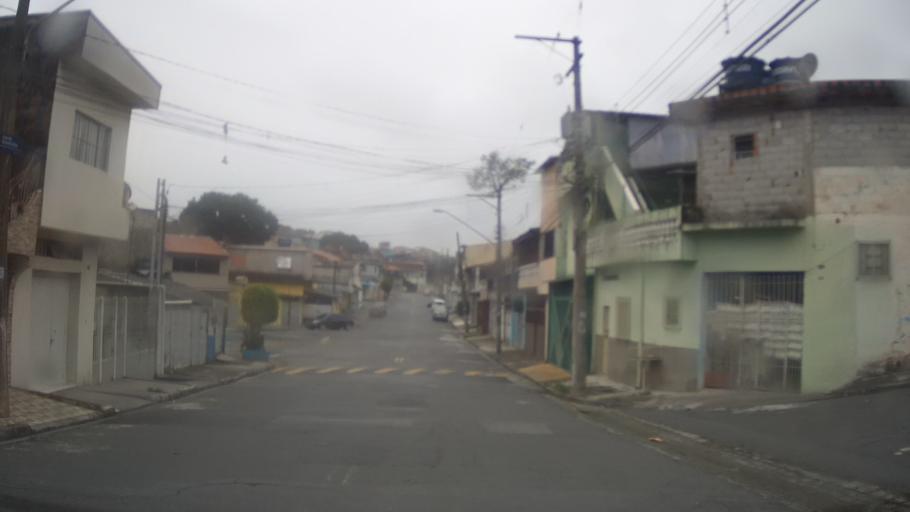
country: BR
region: Sao Paulo
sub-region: Guarulhos
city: Guarulhos
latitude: -23.4381
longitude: -46.5123
